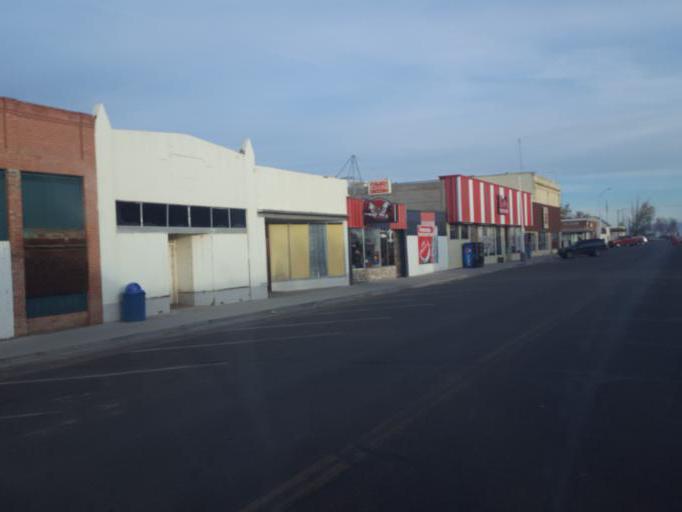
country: US
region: Colorado
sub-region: Saguache County
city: Center
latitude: 37.7524
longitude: -106.1084
